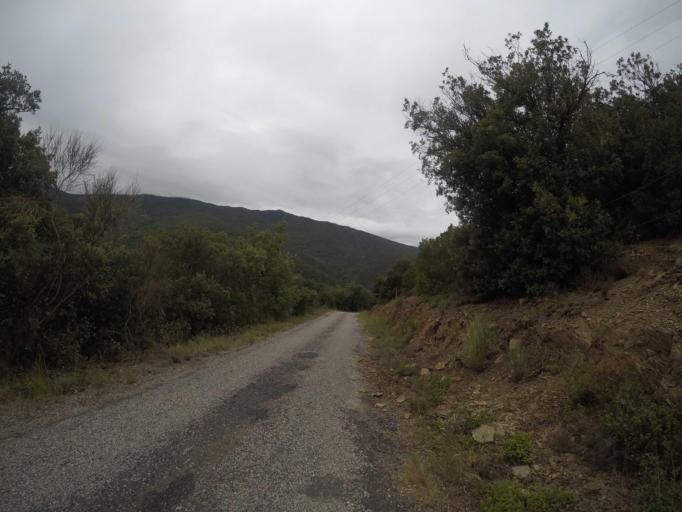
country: FR
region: Languedoc-Roussillon
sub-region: Departement des Pyrenees-Orientales
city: Ille-sur-Tet
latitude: 42.6122
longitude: 2.6098
